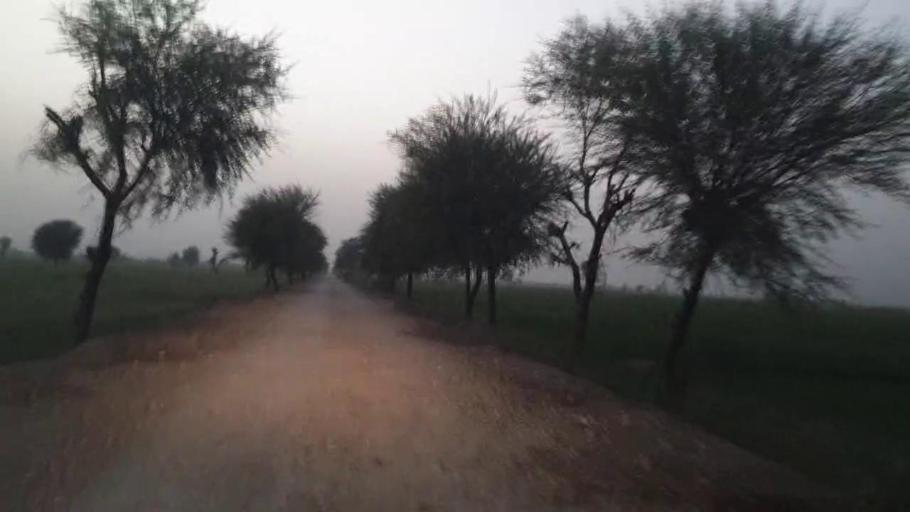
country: PK
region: Sindh
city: Nabisar
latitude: 25.0901
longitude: 69.5784
